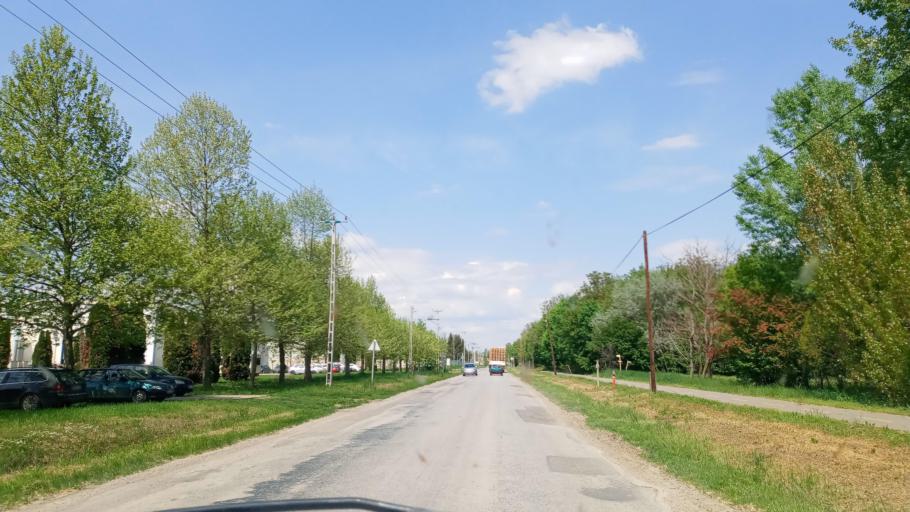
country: HU
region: Baranya
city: Boly
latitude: 45.9573
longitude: 18.5274
